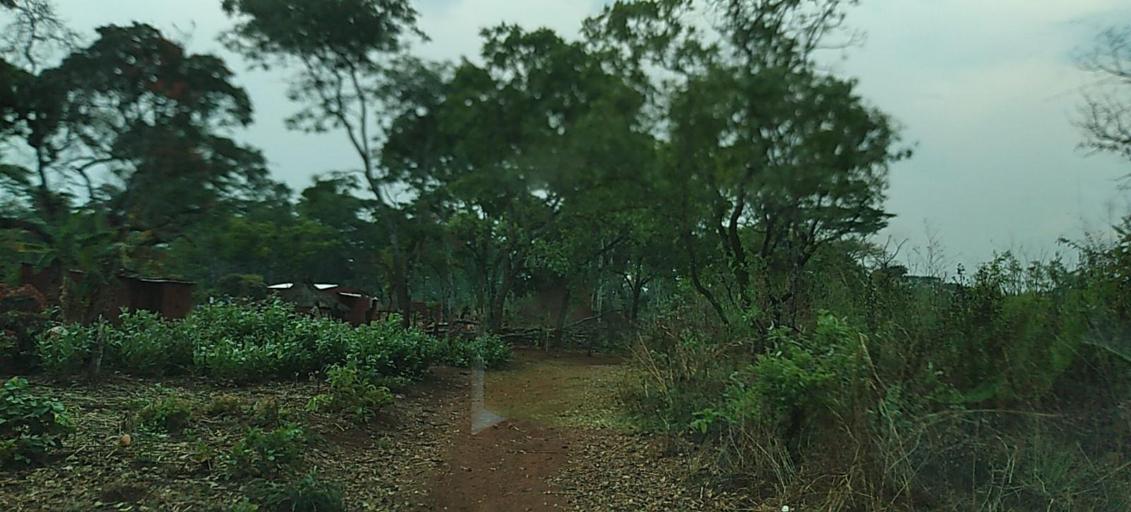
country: ZM
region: North-Western
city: Solwezi
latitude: -12.0451
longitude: 26.0077
